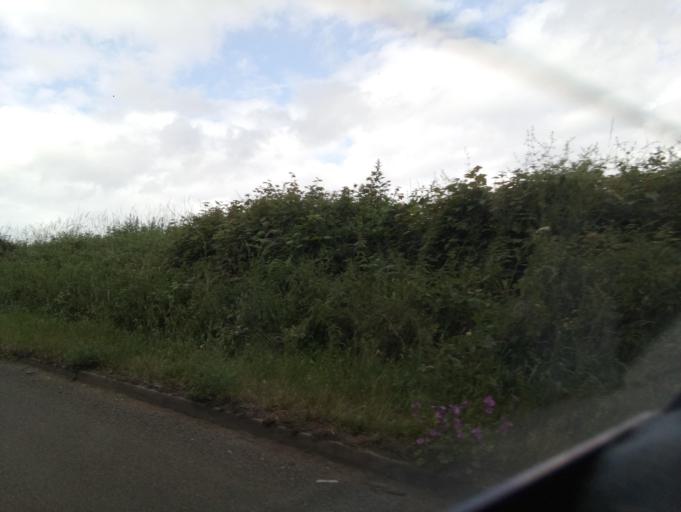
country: GB
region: England
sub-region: Dudley
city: Kingswinford
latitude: 52.4778
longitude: -2.1923
